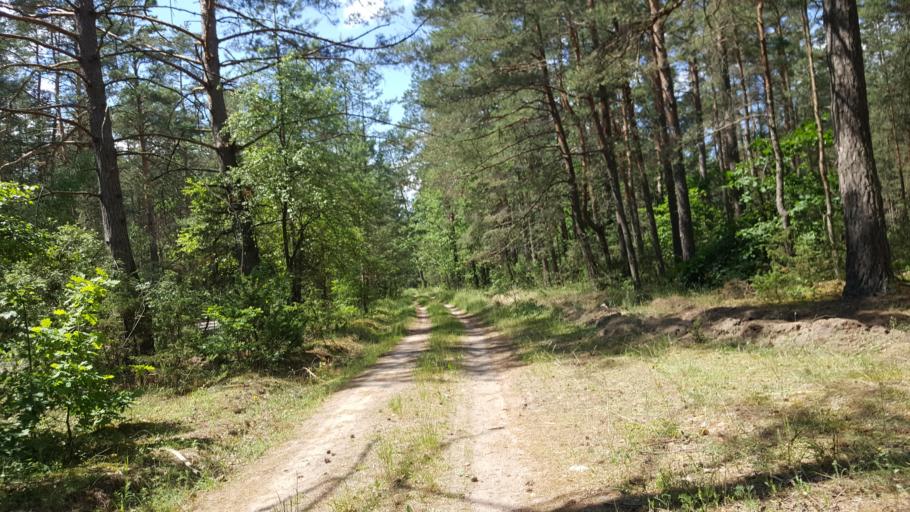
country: BY
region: Brest
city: Kamyanyuki
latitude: 52.5621
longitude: 23.7882
